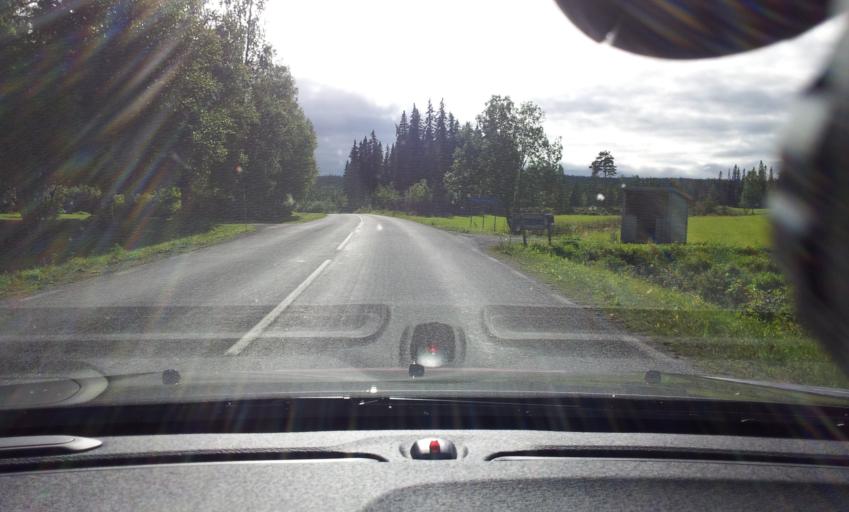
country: SE
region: Jaemtland
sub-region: Krokoms Kommun
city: Krokom
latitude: 63.4855
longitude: 14.1952
